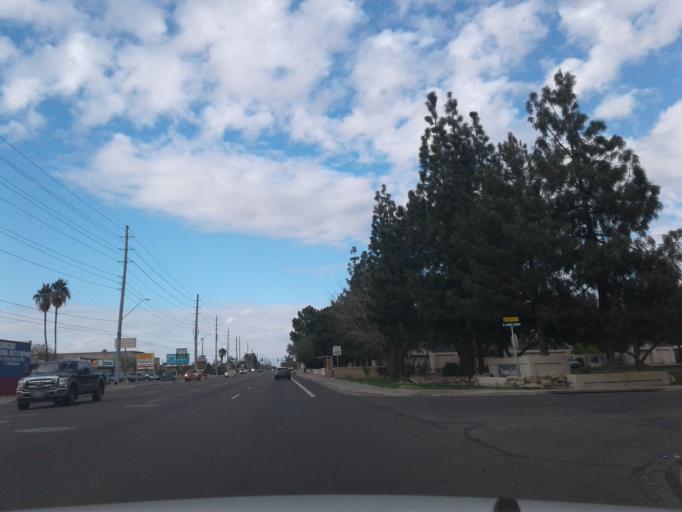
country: US
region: Arizona
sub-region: Maricopa County
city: Paradise Valley
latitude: 33.6375
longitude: -112.0134
